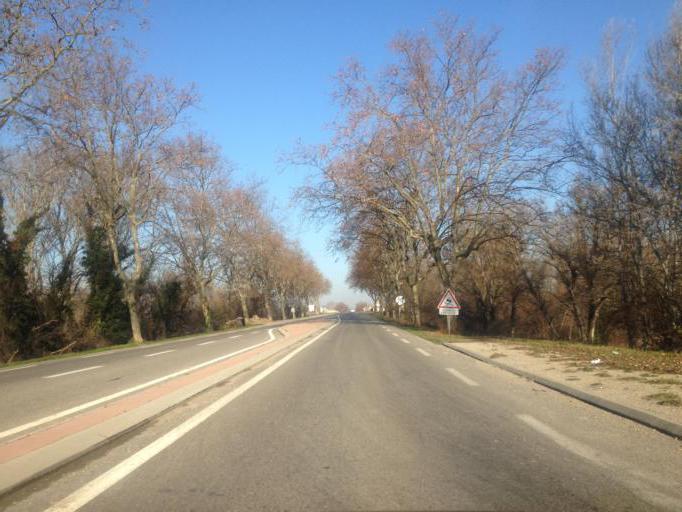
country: FR
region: Provence-Alpes-Cote d'Azur
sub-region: Departement du Vaucluse
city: Mondragon
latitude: 44.2506
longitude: 4.7097
